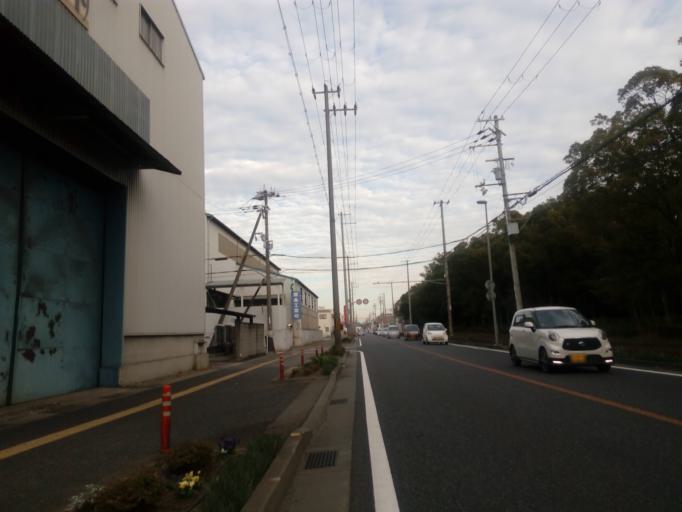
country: JP
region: Hyogo
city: Himeji
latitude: 34.7953
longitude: 134.6263
